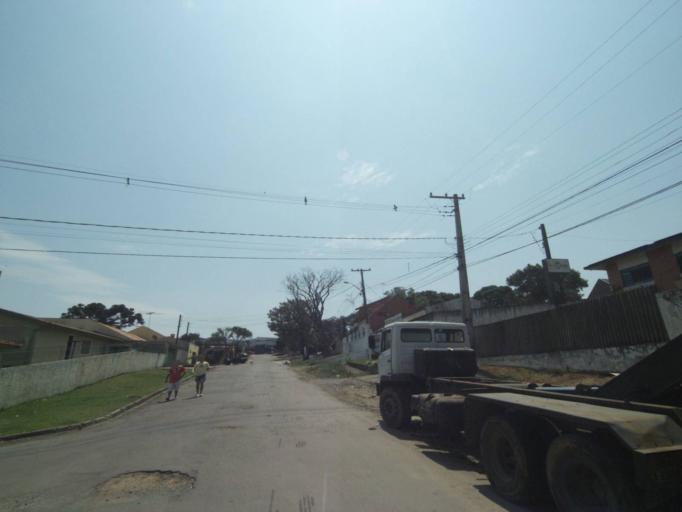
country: BR
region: Parana
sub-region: Curitiba
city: Curitiba
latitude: -25.4804
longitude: -49.3128
